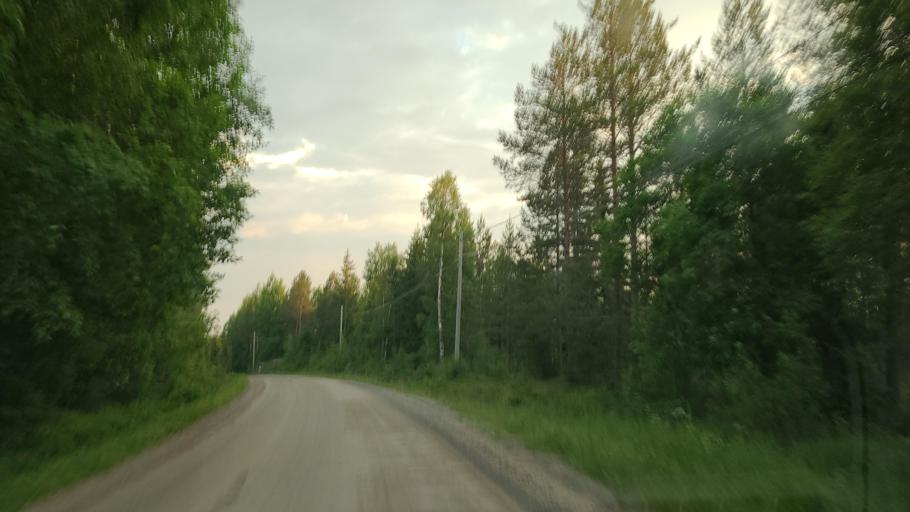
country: SE
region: Vaesterbotten
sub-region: Robertsfors Kommun
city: Robertsfors
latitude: 64.0690
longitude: 20.8736
